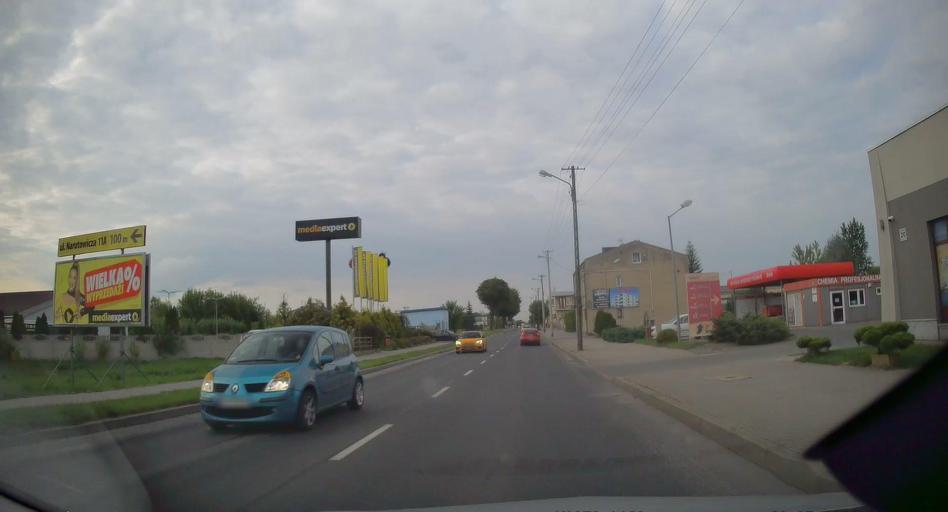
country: PL
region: Lodz Voivodeship
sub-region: Powiat radomszczanski
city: Radomsko
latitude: 51.0737
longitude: 19.4473
